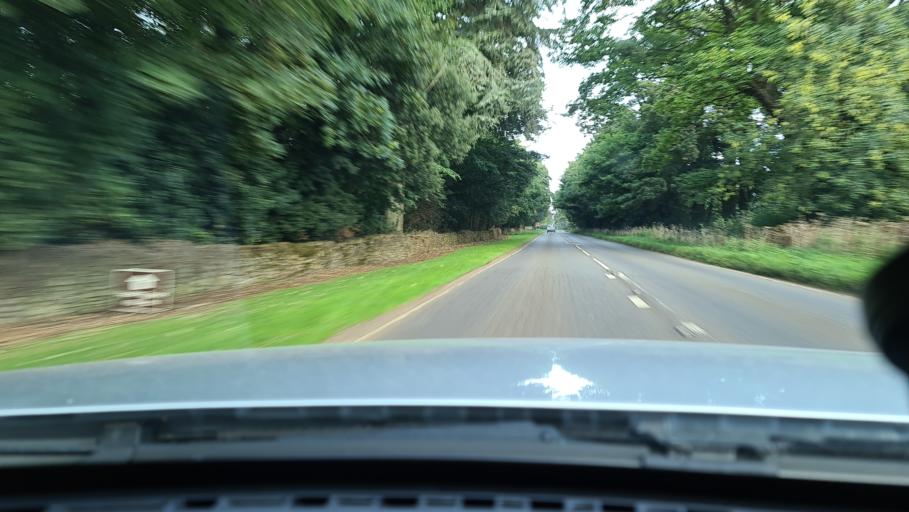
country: GB
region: England
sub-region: Oxfordshire
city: Hanwell
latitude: 52.1095
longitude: -1.4556
